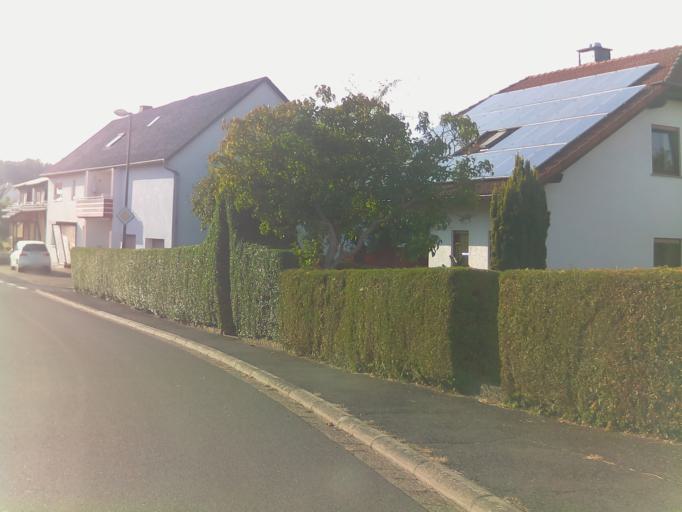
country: DE
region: Hesse
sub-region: Regierungsbezirk Kassel
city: Flieden
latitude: 50.4180
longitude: 9.5024
